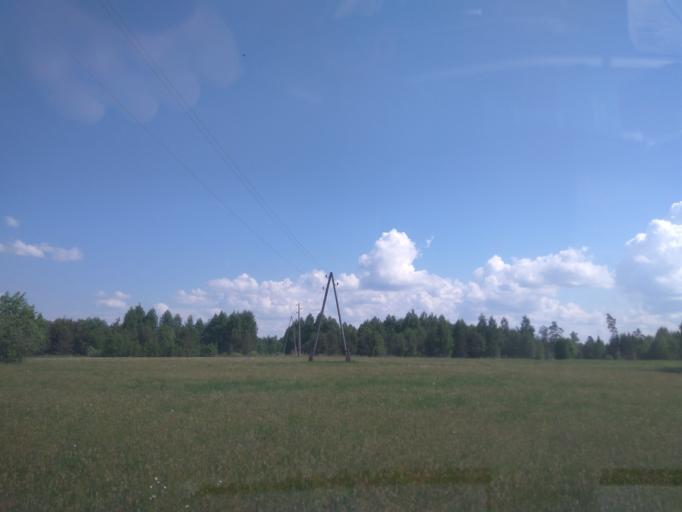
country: LV
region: Kuldigas Rajons
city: Kuldiga
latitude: 57.1761
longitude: 22.0128
